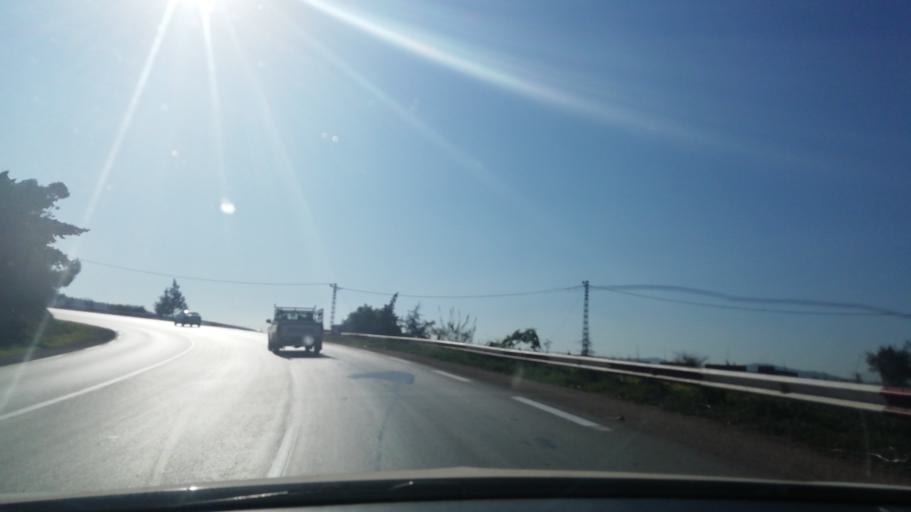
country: DZ
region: Tlemcen
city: Nedroma
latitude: 35.0907
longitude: -1.8271
